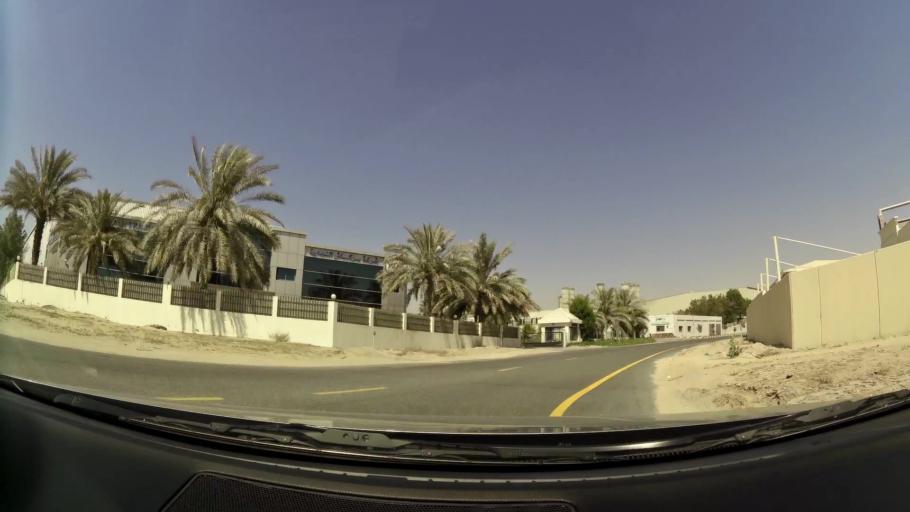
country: AE
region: Dubai
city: Dubai
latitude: 24.9724
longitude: 55.1767
